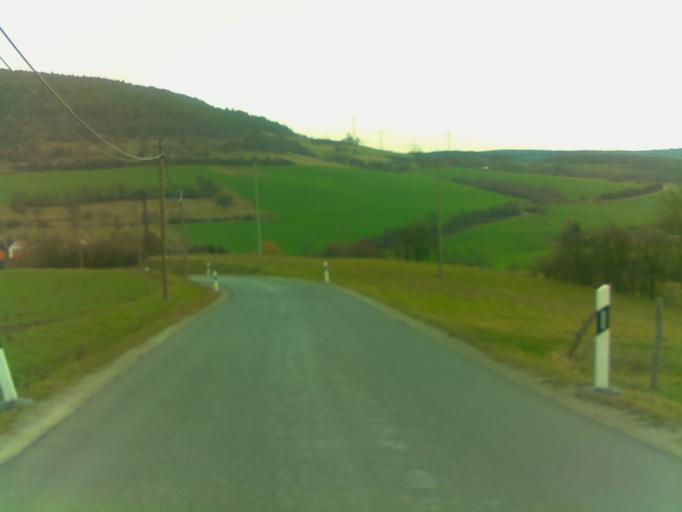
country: DE
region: Thuringia
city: Orlamunde
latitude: 50.7846
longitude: 11.5064
